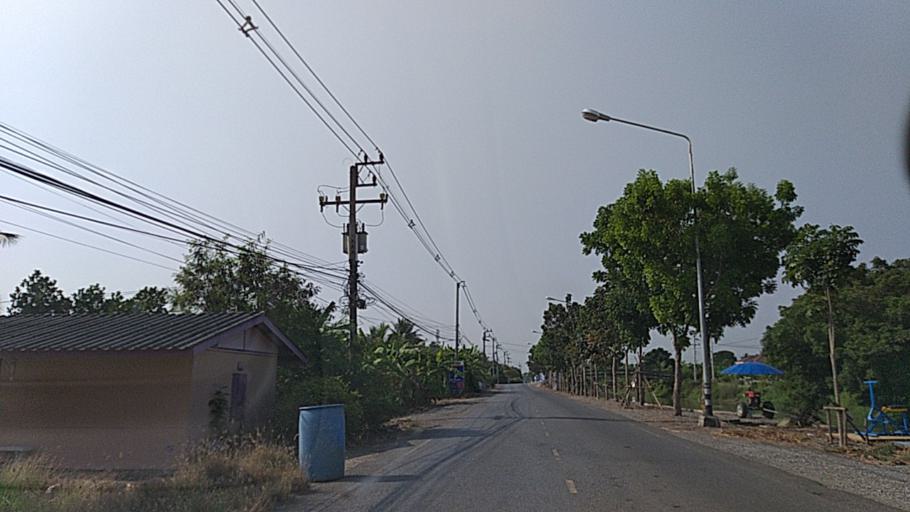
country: TH
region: Pathum Thani
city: Lam Luk Ka
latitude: 13.9631
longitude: 100.7060
